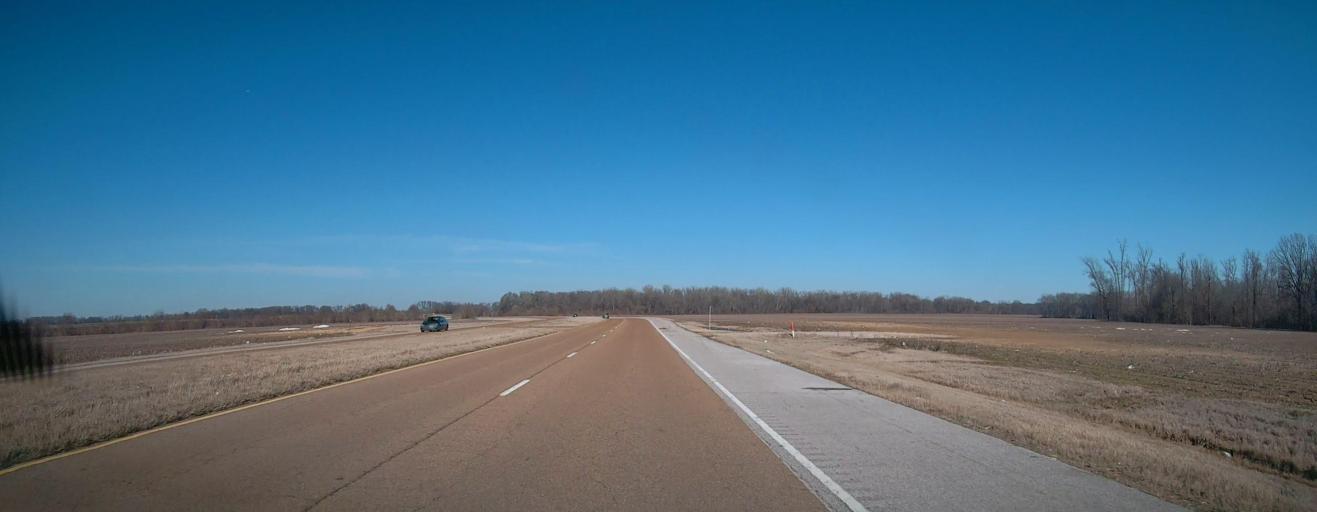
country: US
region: Tennessee
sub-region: Shelby County
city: Millington
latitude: 35.2827
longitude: -89.8827
